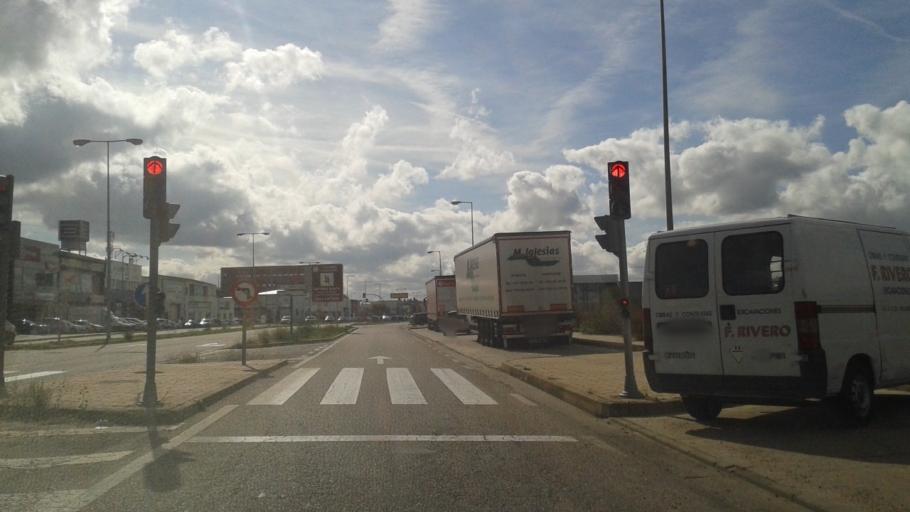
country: ES
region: Castille and Leon
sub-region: Provincia de Valladolid
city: Valladolid
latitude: 41.6734
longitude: -4.7245
